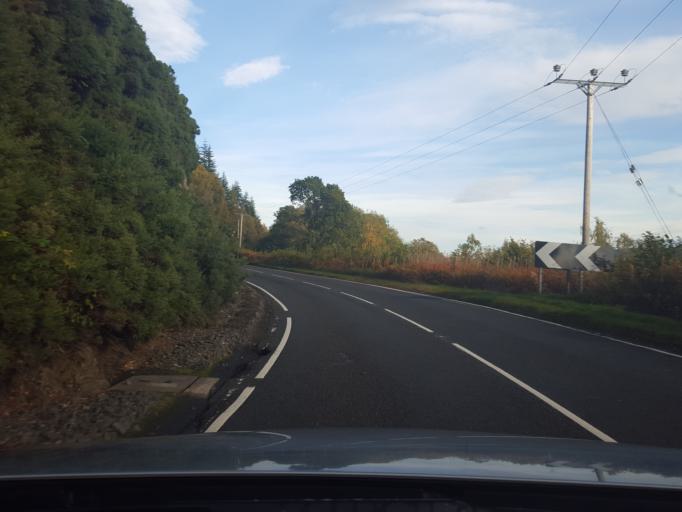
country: GB
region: Scotland
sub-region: Highland
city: Beauly
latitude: 57.2201
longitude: -4.5806
